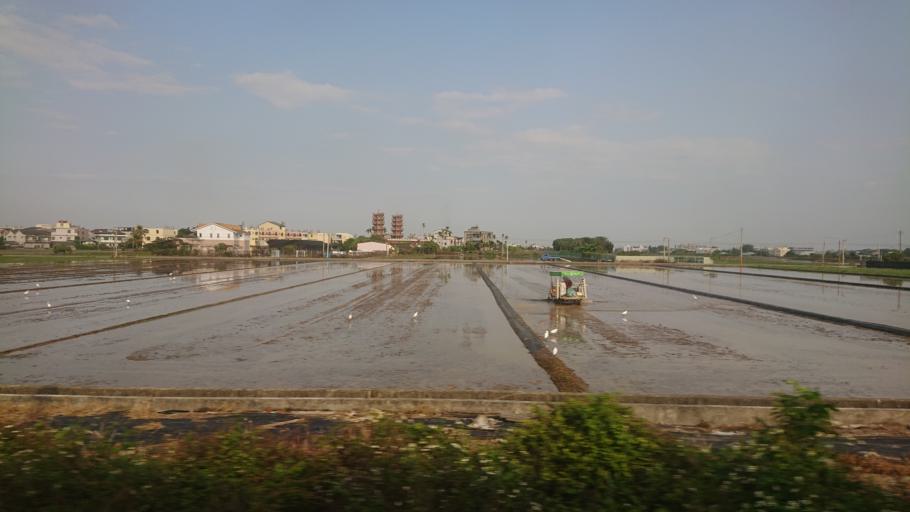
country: TW
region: Taiwan
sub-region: Yunlin
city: Douliu
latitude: 23.6937
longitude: 120.5119
